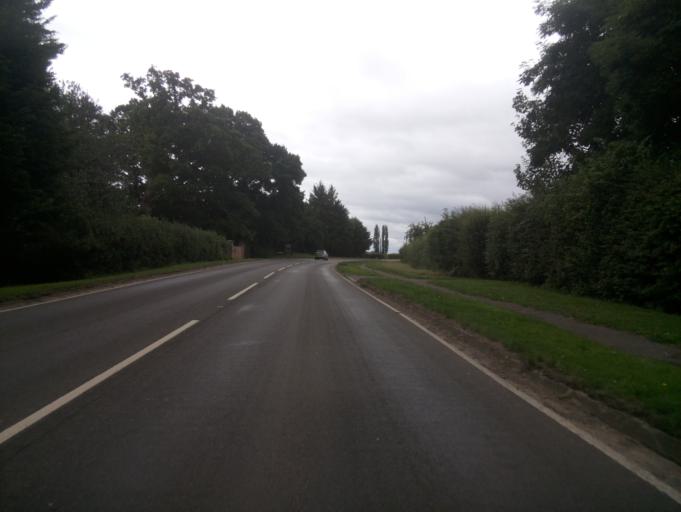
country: GB
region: England
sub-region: Worcestershire
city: Kempsey
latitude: 52.1318
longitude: -2.2151
